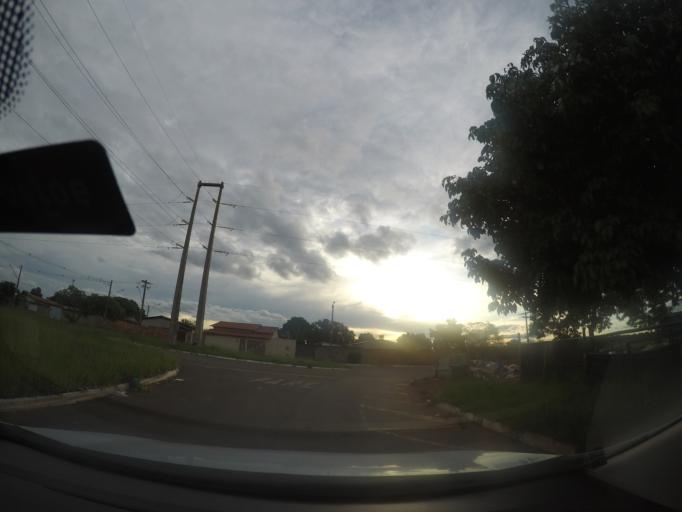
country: BR
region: Goias
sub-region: Goianira
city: Goianira
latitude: -16.5852
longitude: -49.3773
